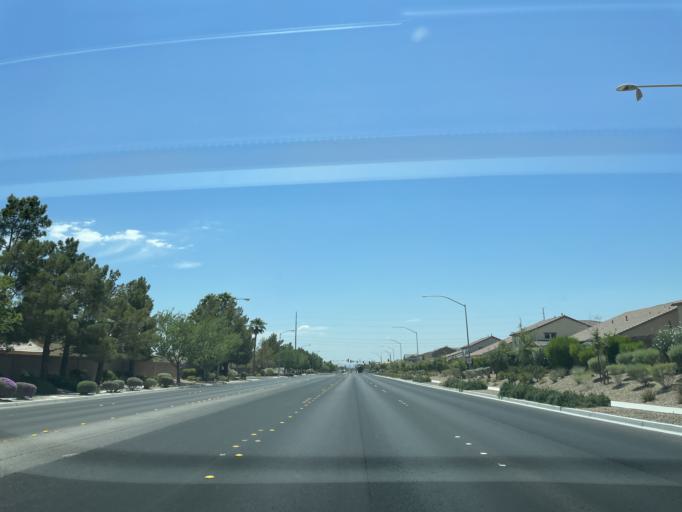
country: US
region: Nevada
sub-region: Clark County
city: North Las Vegas
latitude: 36.2794
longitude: -115.1532
